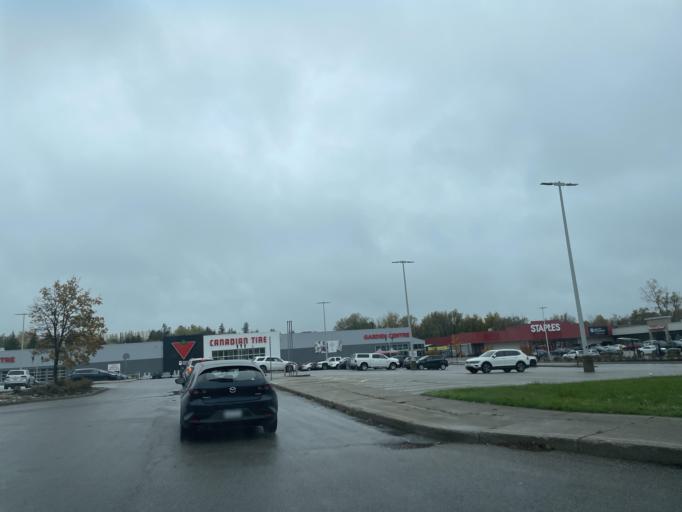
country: CA
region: Ontario
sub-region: Wellington County
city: Guelph
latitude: 43.5662
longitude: -80.2762
